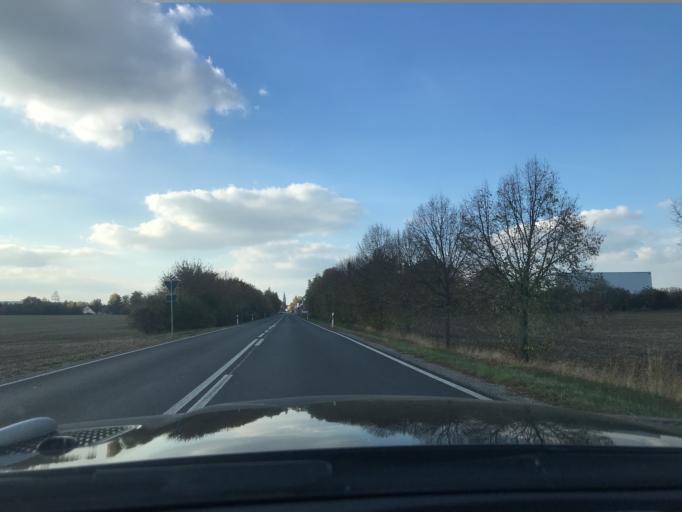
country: DE
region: Thuringia
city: Bad Langensalza
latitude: 51.1020
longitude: 10.6729
